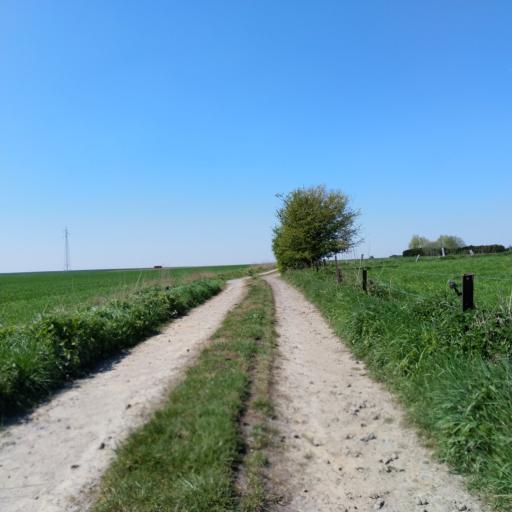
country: BE
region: Wallonia
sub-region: Province du Hainaut
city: Lens
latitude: 50.5606
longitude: 3.8912
